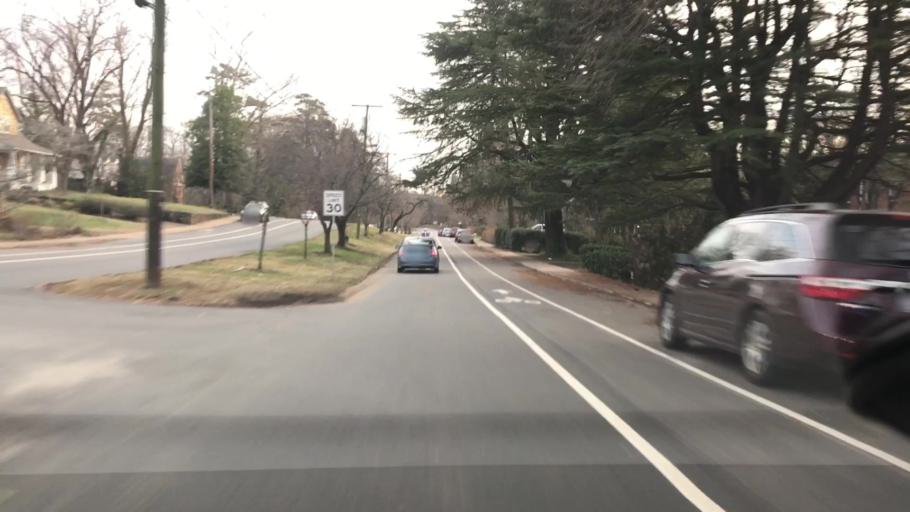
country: US
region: Virginia
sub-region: City of Charlottesville
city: Charlottesville
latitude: 38.0235
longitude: -78.5150
